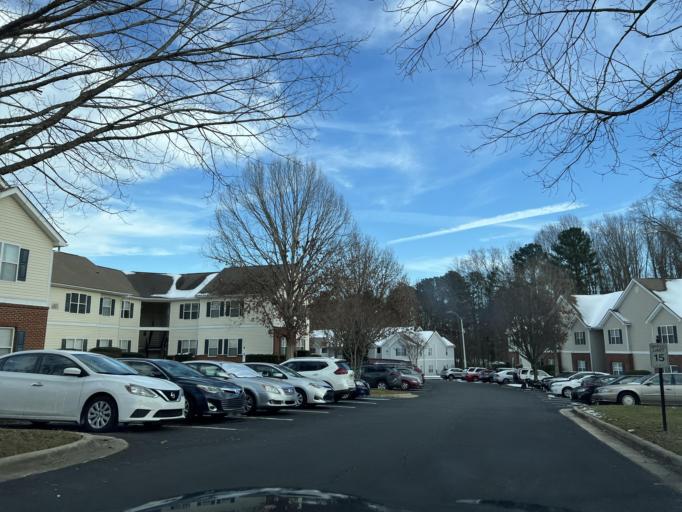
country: US
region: North Carolina
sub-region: Wake County
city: Raleigh
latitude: 35.8706
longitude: -78.5885
